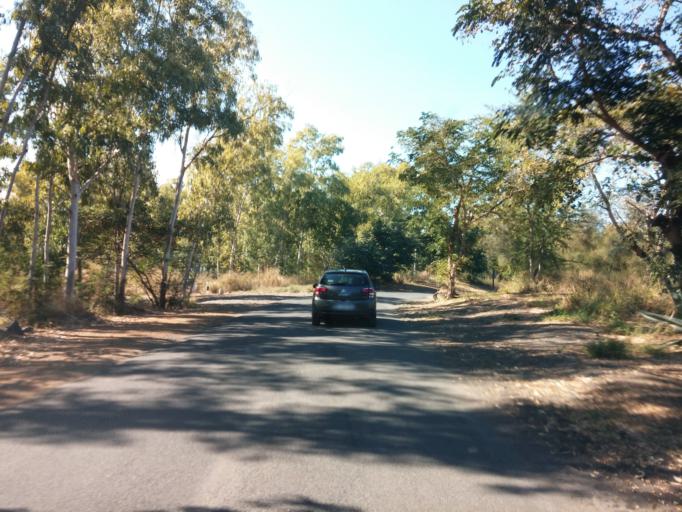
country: RE
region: Reunion
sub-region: Reunion
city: Les Avirons
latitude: -21.2713
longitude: 55.3530
